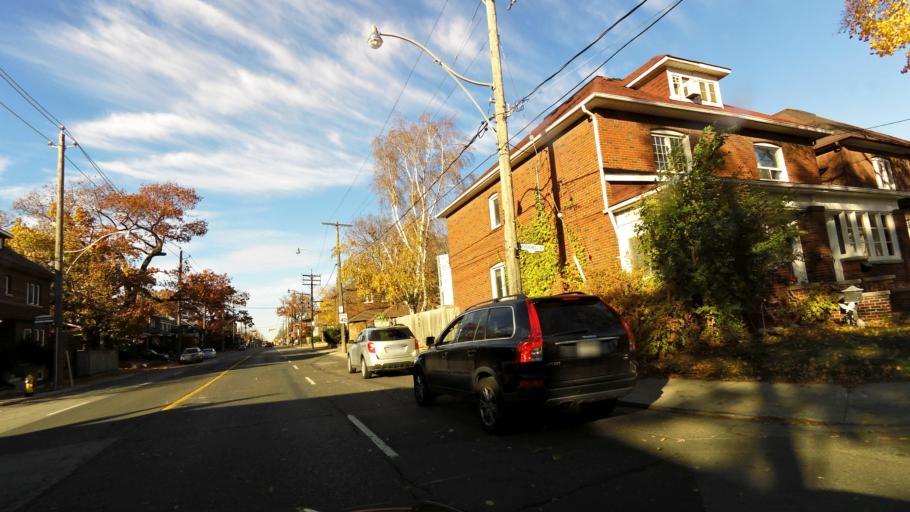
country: CA
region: Ontario
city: Etobicoke
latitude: 43.6515
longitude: -79.4854
